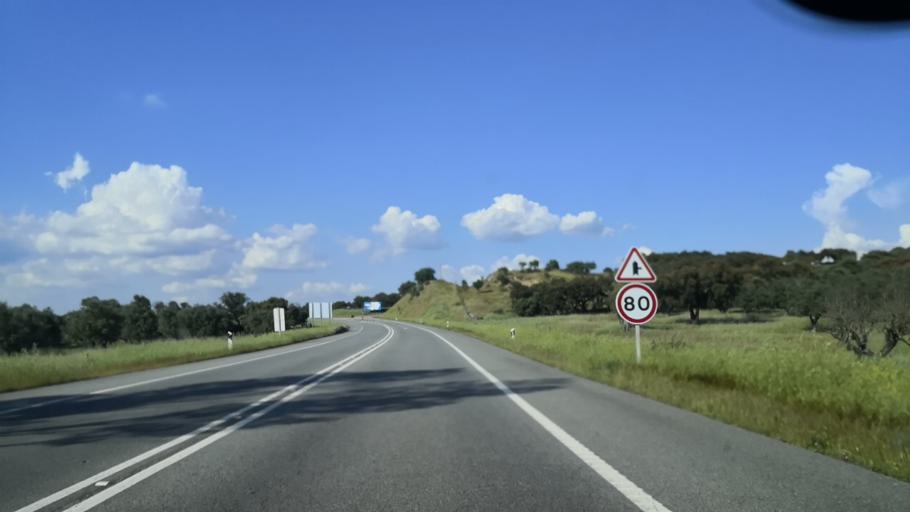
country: PT
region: Portalegre
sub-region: Arronches
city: Arronches
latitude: 39.0597
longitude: -7.4398
